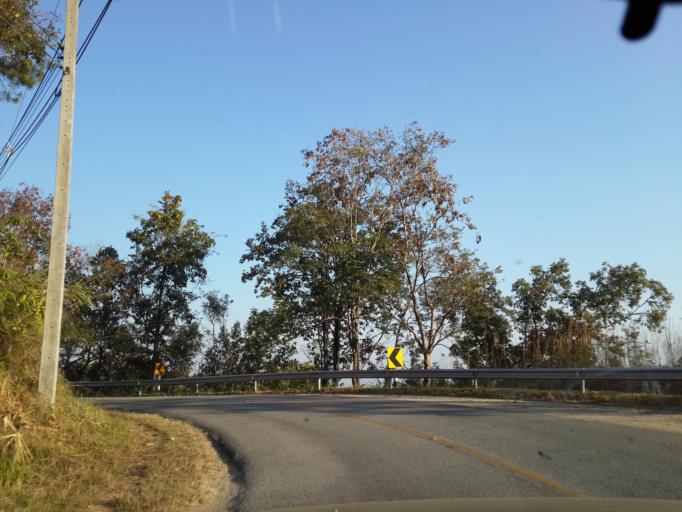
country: TH
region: Chiang Mai
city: Chai Prakan
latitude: 19.8354
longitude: 99.0930
